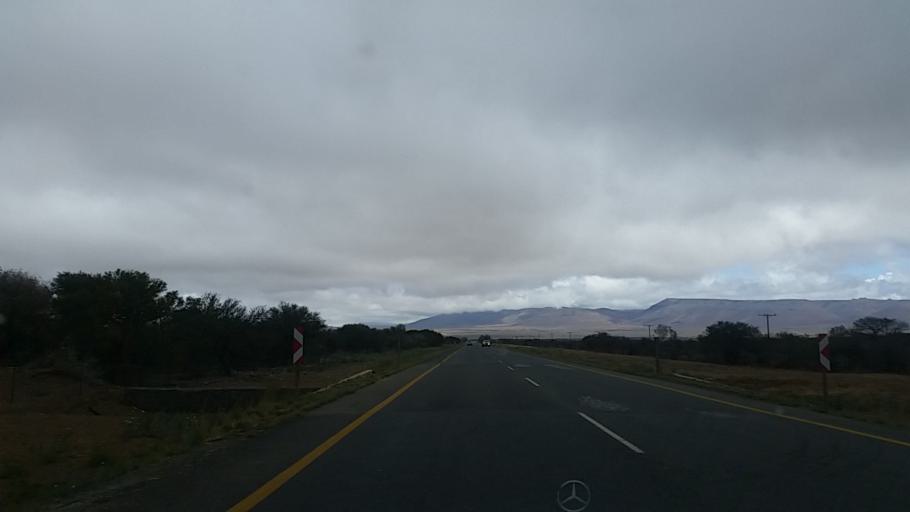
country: ZA
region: Eastern Cape
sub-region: Cacadu District Municipality
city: Graaff-Reinet
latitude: -31.9822
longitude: 24.6979
